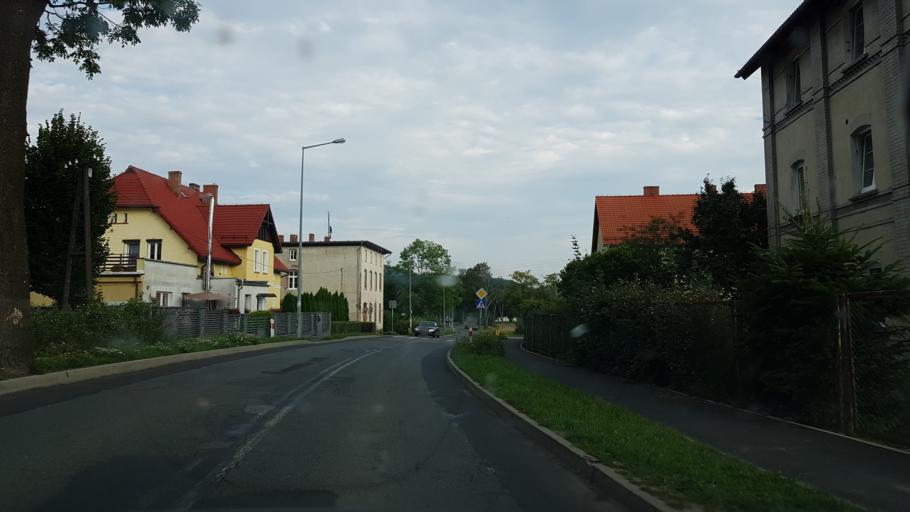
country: PL
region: Lower Silesian Voivodeship
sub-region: Powiat kamiennogorski
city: Marciszow
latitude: 50.8526
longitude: 16.0085
